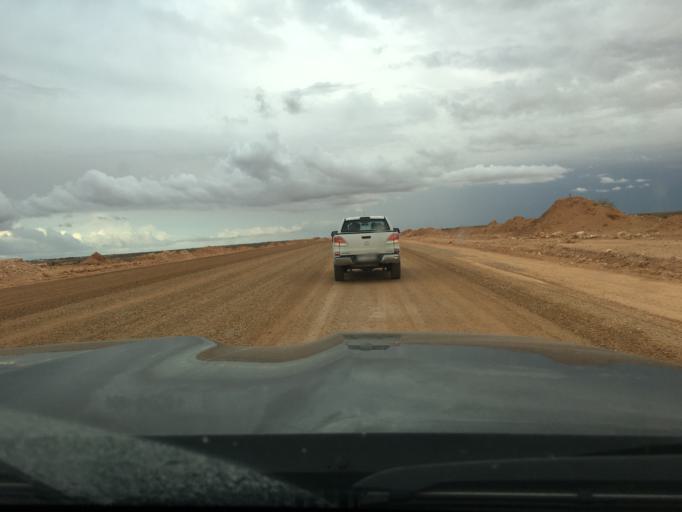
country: TN
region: Madanin
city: Medenine
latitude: 33.2646
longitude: 10.5810
